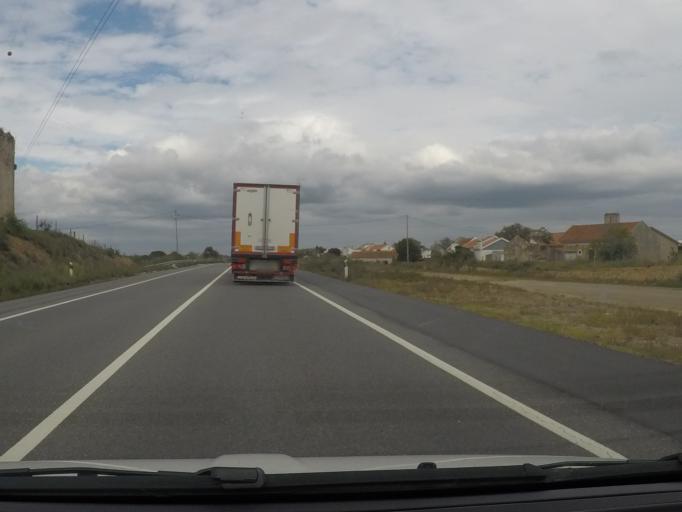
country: PT
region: Setubal
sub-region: Santiago do Cacem
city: Santiago do Cacem
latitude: 38.0722
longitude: -8.6530
